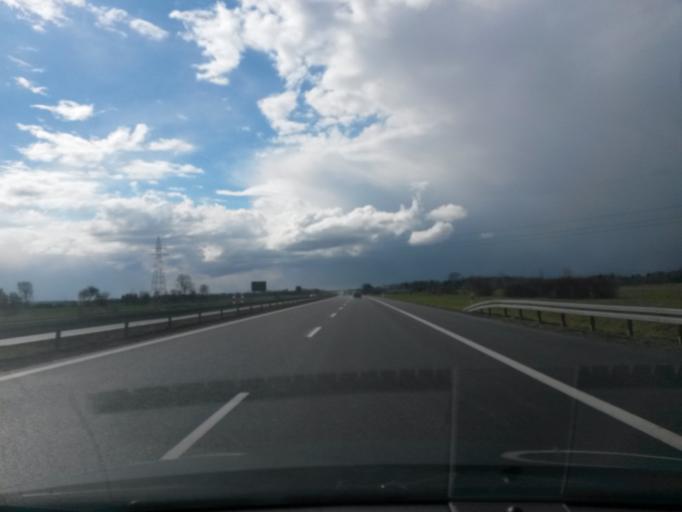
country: PL
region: Greater Poland Voivodeship
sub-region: Powiat wrzesinski
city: Wrzesnia
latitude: 52.3181
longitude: 17.5090
